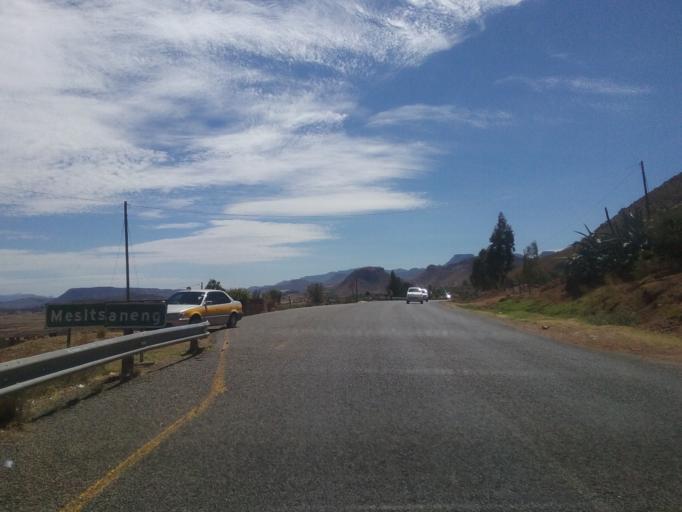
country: LS
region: Mohale's Hoek District
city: Mohale's Hoek
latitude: -30.1881
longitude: 27.4179
